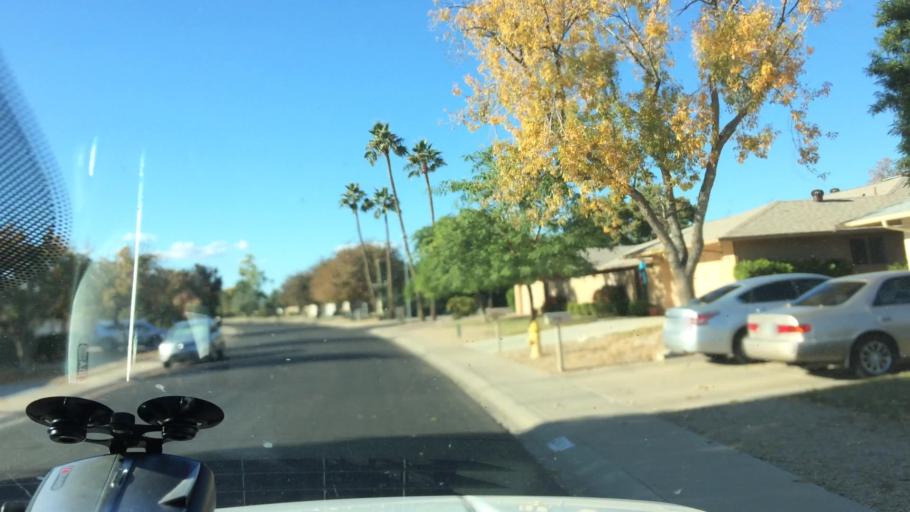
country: US
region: Arizona
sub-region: Maricopa County
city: Sun City West
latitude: 33.6525
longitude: -112.3353
